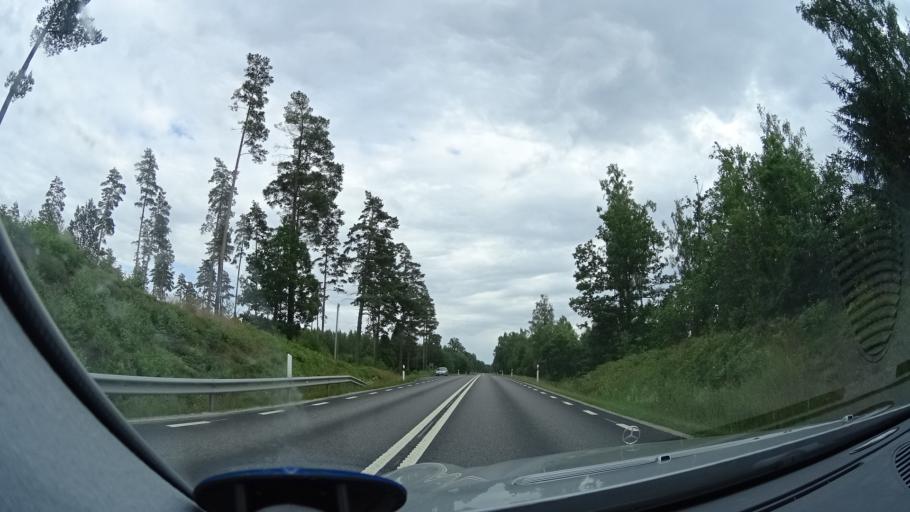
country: SE
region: Kronoberg
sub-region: Tingsryds Kommun
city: Tingsryd
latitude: 56.4948
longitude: 14.9972
